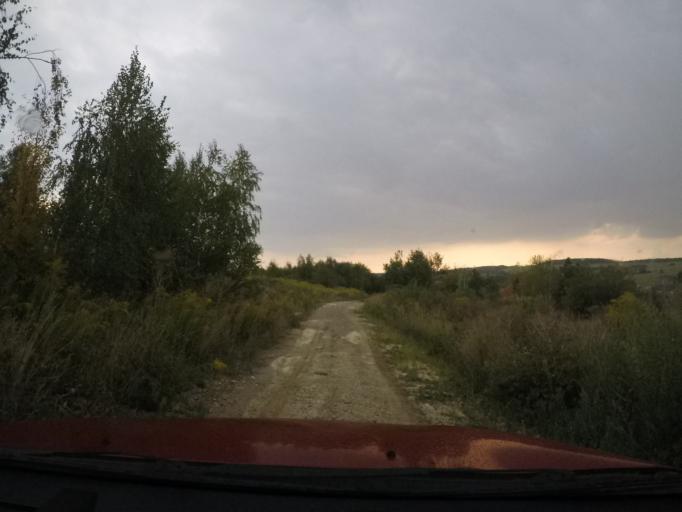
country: SK
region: Kosicky
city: Kosice
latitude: 48.6887
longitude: 21.1972
